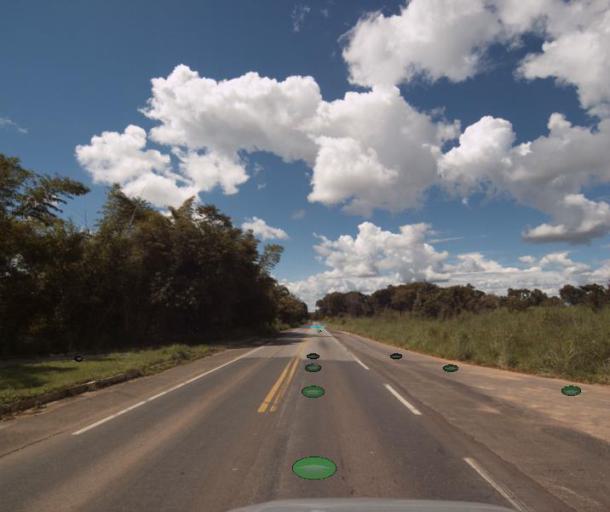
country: BR
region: Goias
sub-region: Porangatu
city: Porangatu
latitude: -13.7305
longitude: -49.0244
